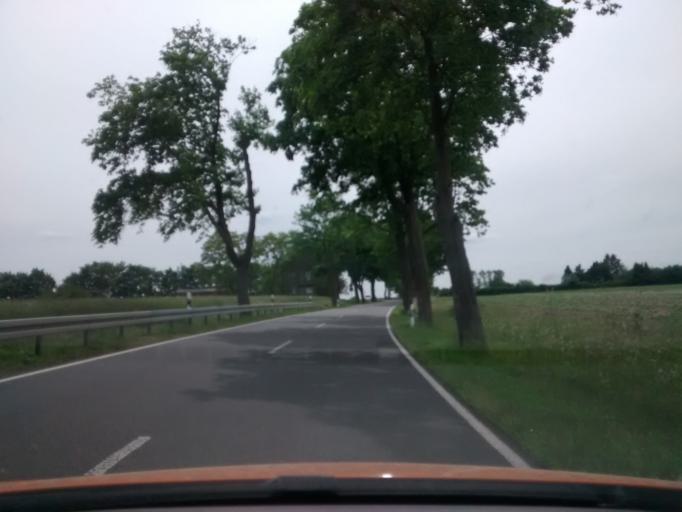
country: DE
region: Brandenburg
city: Juterbog
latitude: 51.9107
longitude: 13.1370
